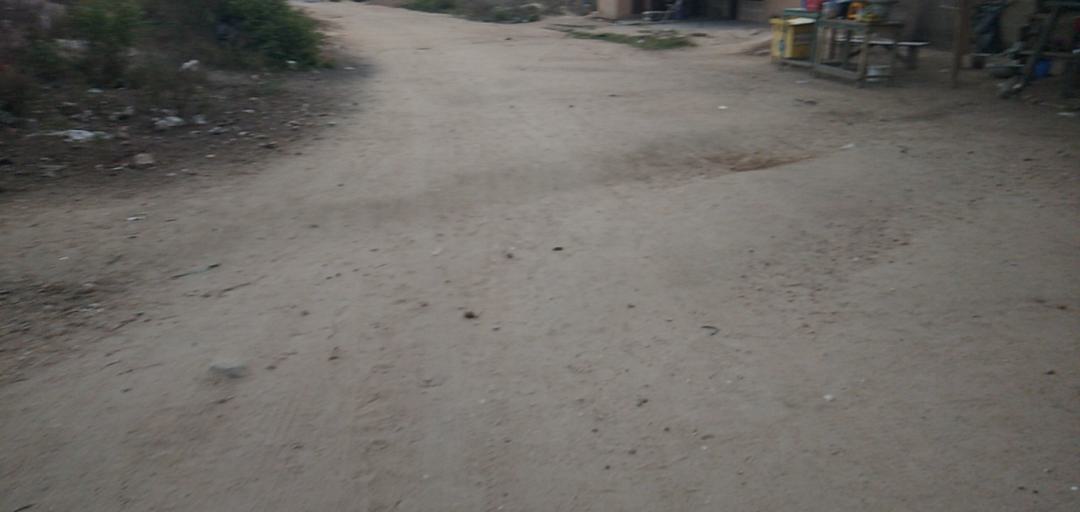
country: GH
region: Central
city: Winneba
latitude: 5.3523
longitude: -0.6147
